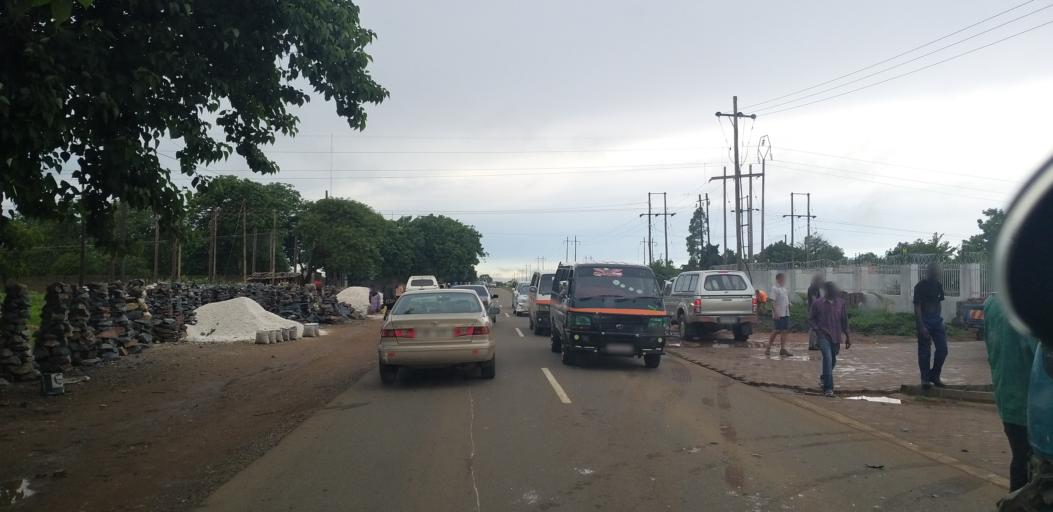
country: ZM
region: Lusaka
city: Lusaka
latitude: -15.4397
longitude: 28.3614
